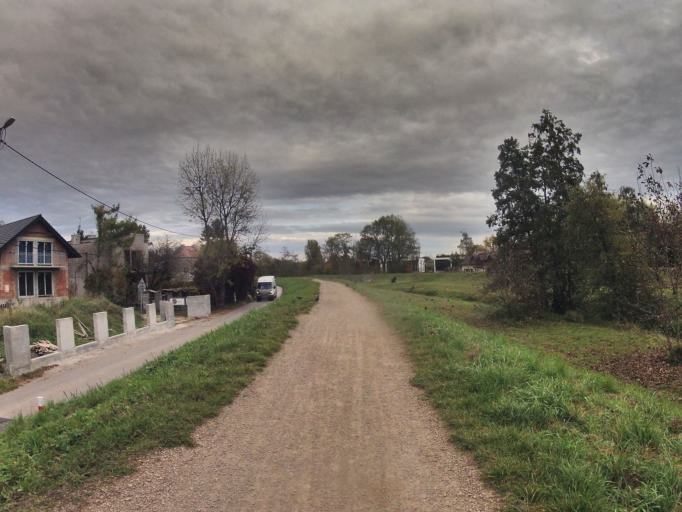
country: PL
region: Lesser Poland Voivodeship
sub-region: Powiat krakowski
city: Rzaska
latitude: 50.0679
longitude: 19.8825
